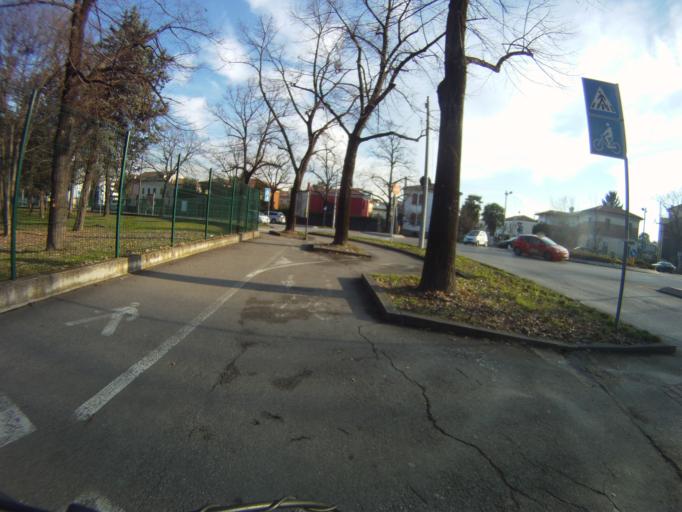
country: IT
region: Veneto
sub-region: Provincia di Padova
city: Padova
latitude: 45.4021
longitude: 11.8892
